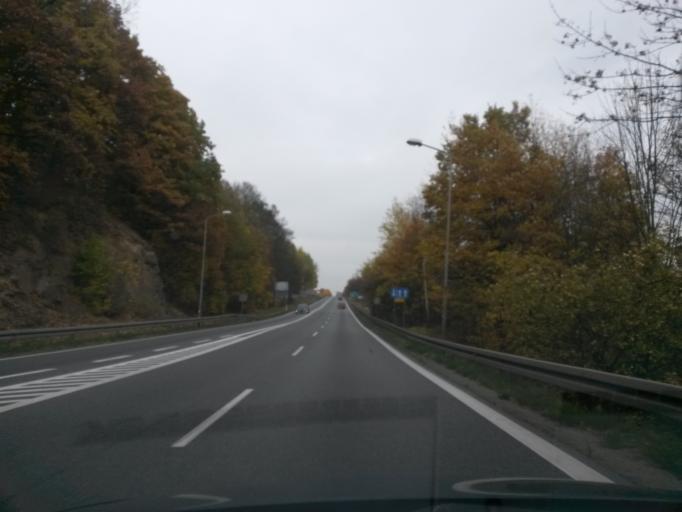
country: PL
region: Lower Silesian Voivodeship
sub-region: Powiat klodzki
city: Klodzko
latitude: 50.4585
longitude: 16.6725
